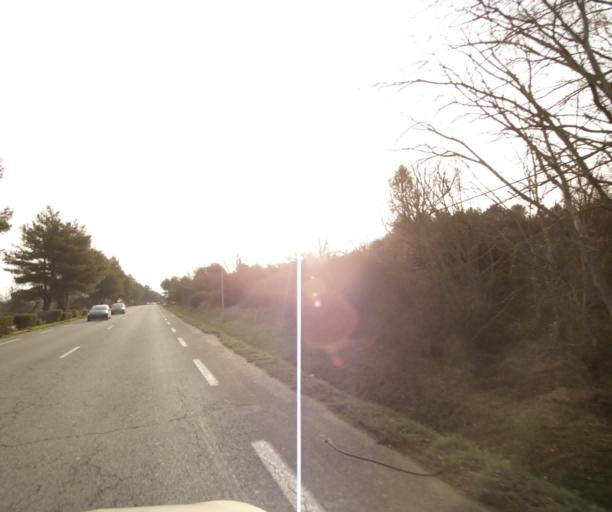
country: FR
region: Provence-Alpes-Cote d'Azur
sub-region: Departement des Bouches-du-Rhone
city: Peynier
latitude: 43.4610
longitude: 5.6334
